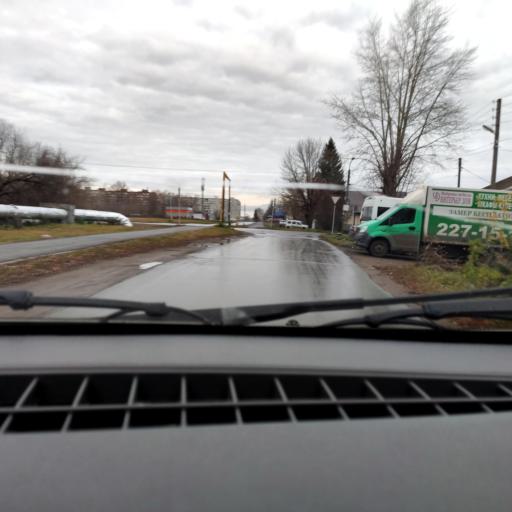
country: RU
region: Bashkortostan
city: Avdon
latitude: 54.7019
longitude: 55.8189
